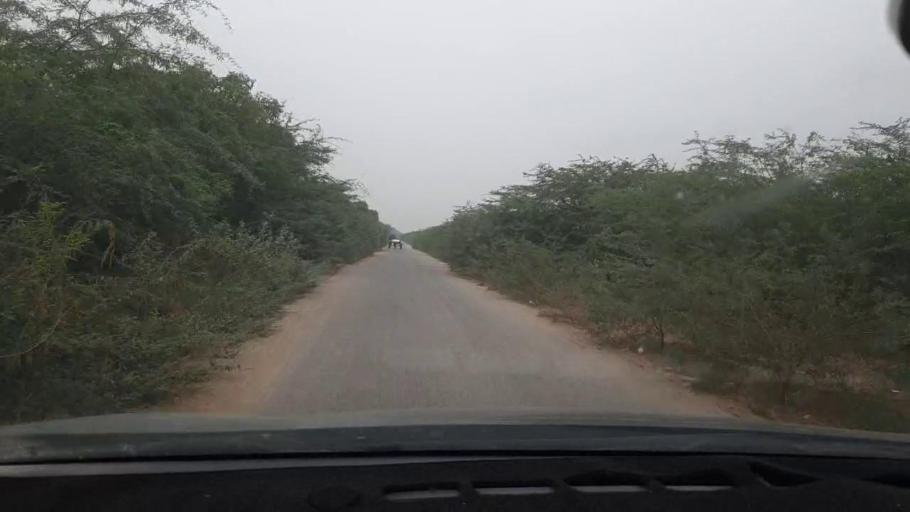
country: PK
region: Sindh
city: Malir Cantonment
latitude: 24.9254
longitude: 67.3261
